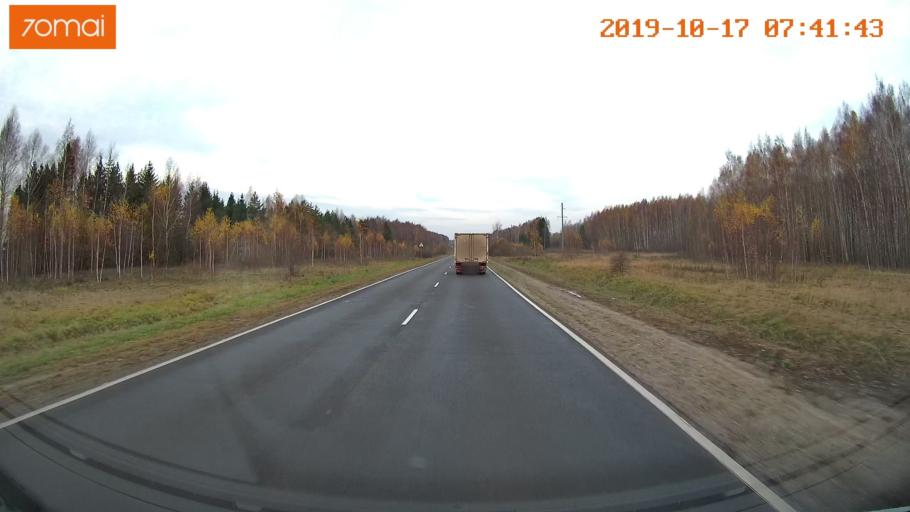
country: RU
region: Vladimir
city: Yur'yev-Pol'skiy
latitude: 56.4833
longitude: 39.8044
